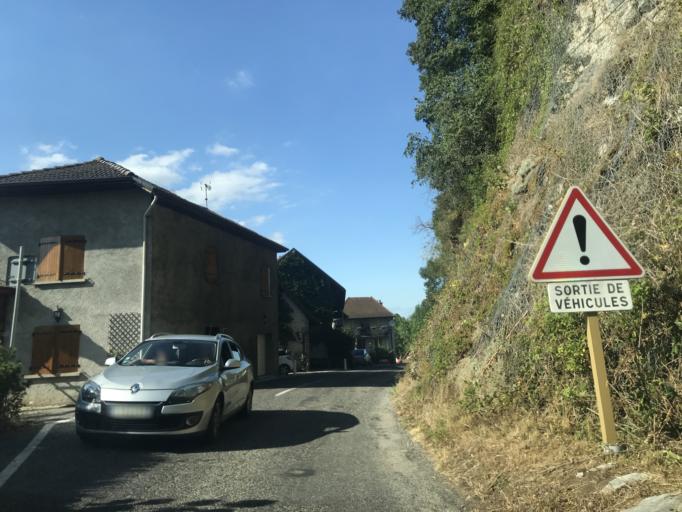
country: FR
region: Rhone-Alpes
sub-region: Departement de l'Ain
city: Culoz
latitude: 45.8082
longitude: 5.7880
